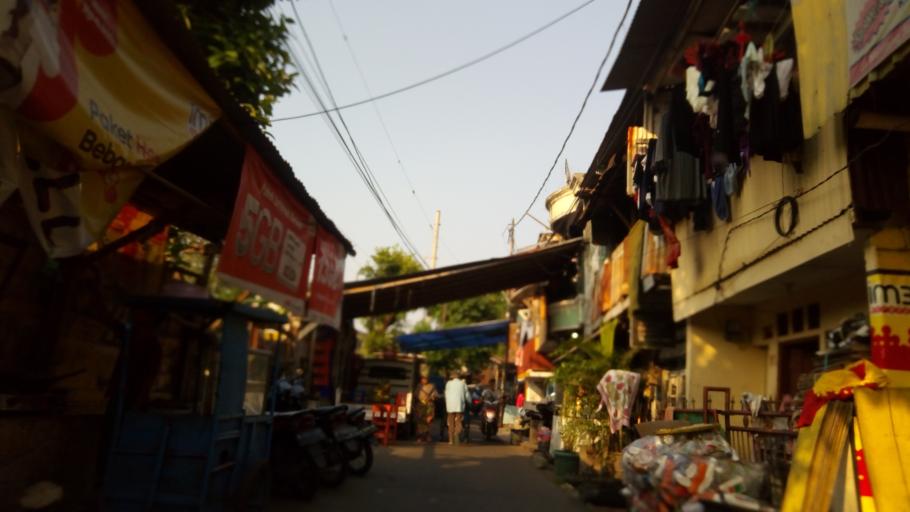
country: ID
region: Jakarta Raya
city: Jakarta
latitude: -6.2059
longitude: 106.8441
